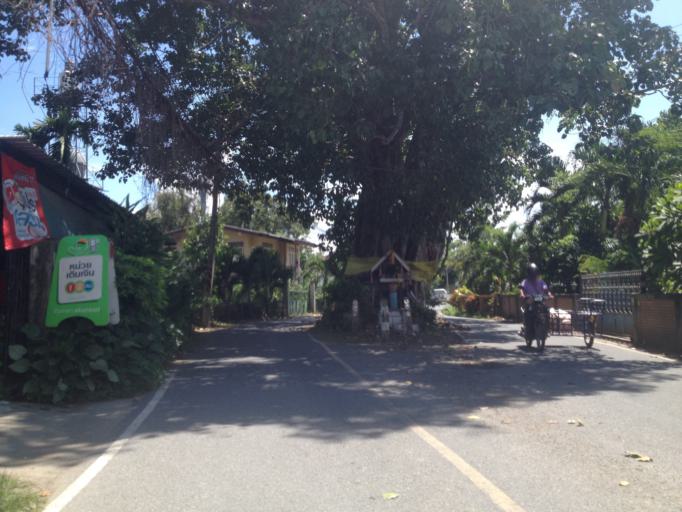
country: TH
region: Chiang Mai
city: Hang Dong
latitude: 18.6822
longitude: 98.9281
